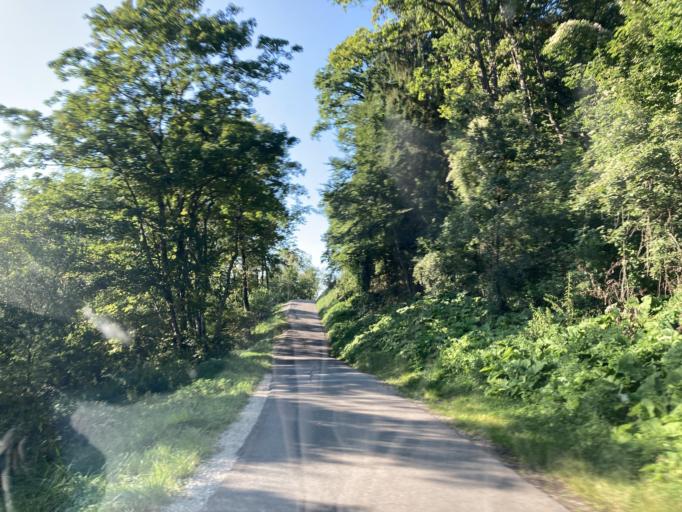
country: DE
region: Baden-Wuerttemberg
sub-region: Freiburg Region
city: Blumberg
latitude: 47.8256
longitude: 8.5100
